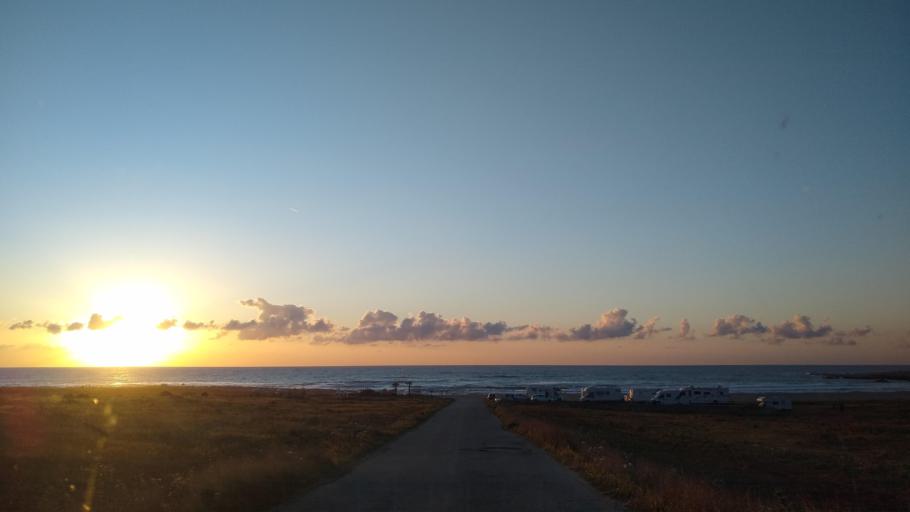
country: IT
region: Sicily
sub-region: Trapani
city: Castelluzzo
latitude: 38.1229
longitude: 12.7304
